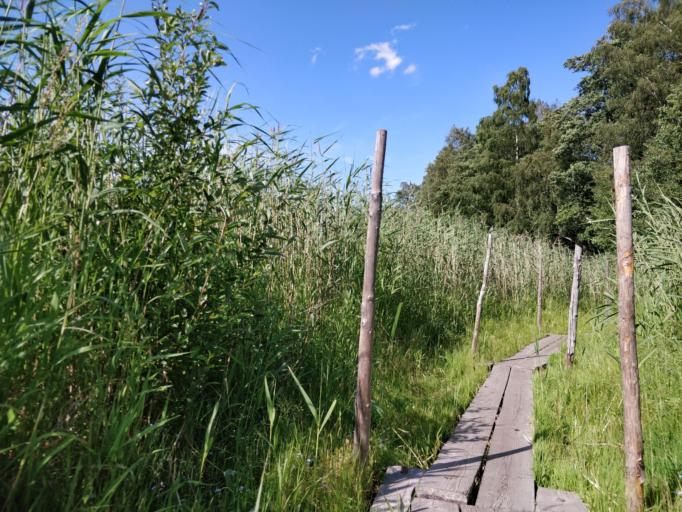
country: FI
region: Uusimaa
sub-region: Helsinki
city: Helsinki
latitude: 60.2066
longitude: 24.9959
